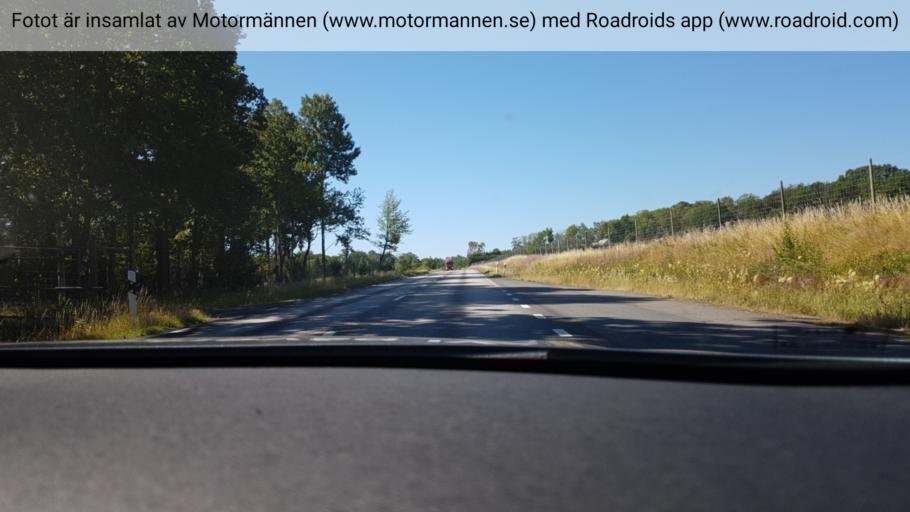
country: SE
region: Joenkoeping
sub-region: Habo Kommun
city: Habo
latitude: 58.0892
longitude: 14.1998
